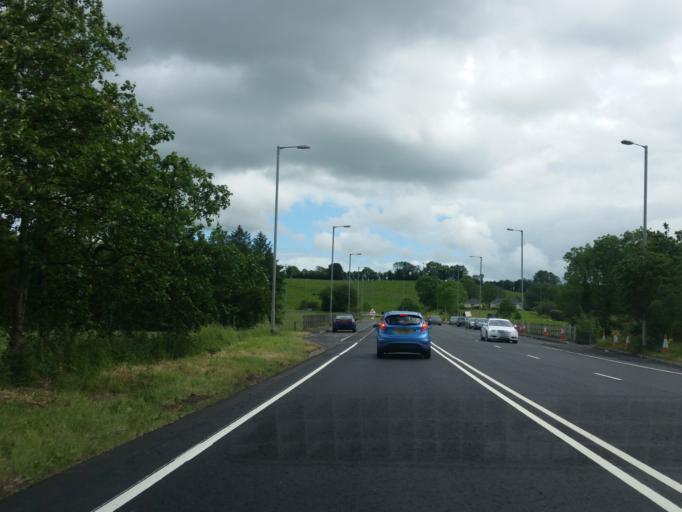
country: IE
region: Ulster
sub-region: County Monaghan
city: Monaghan
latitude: 54.4598
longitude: -7.0341
